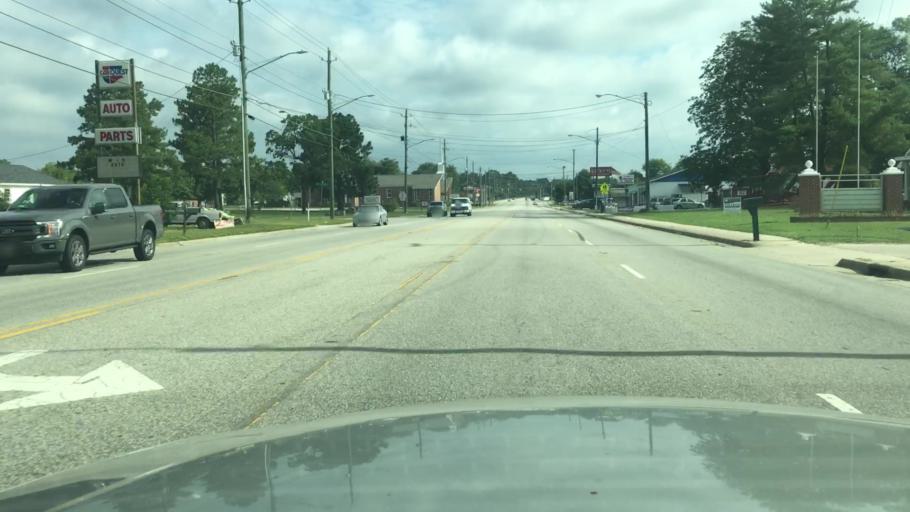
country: US
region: North Carolina
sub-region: Cumberland County
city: Hope Mills
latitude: 35.0009
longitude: -78.9673
